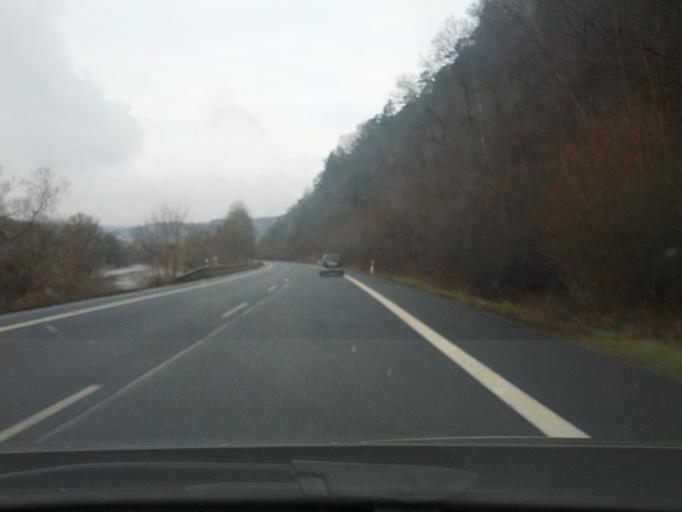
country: DE
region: Lower Saxony
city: Hannoversch Munden
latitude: 51.4140
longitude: 9.6822
